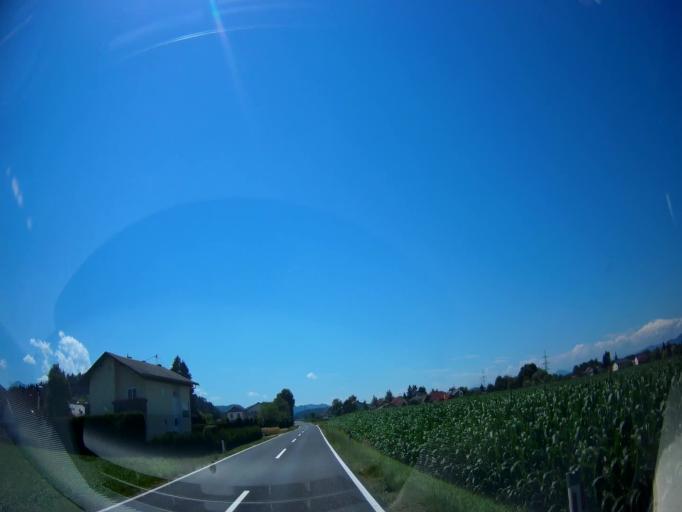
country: AT
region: Carinthia
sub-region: Politischer Bezirk Volkermarkt
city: Eberndorf
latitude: 46.6179
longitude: 14.6021
